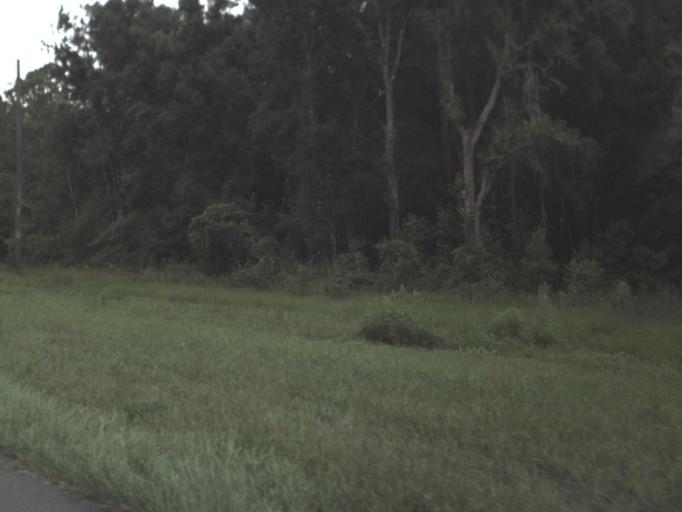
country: US
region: Florida
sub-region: Pasco County
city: Zephyrhills North
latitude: 28.2672
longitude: -82.0899
